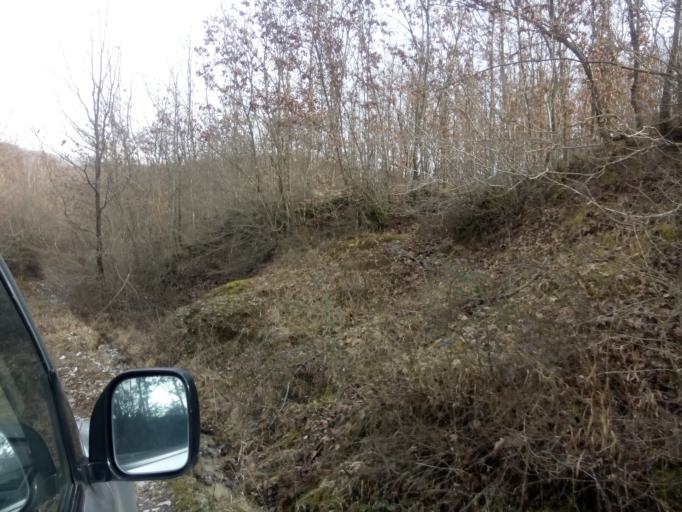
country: AL
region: Diber
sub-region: Rrethi i Matit
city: Rukaj
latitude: 41.6851
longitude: 19.9965
